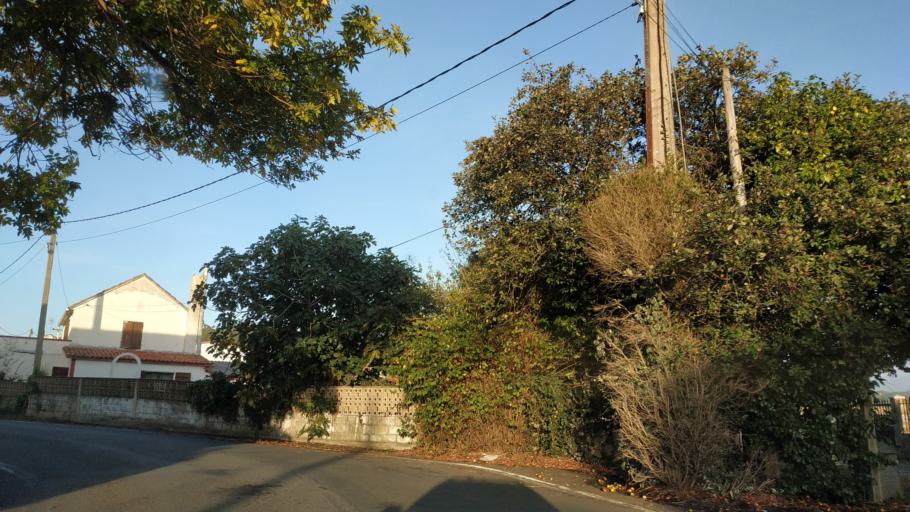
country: ES
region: Galicia
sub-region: Provincia da Coruna
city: Oleiros
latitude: 43.3630
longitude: -8.3392
